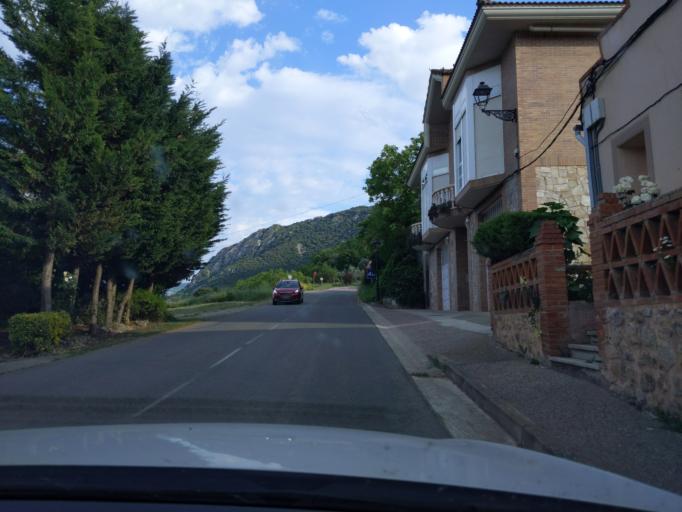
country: ES
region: La Rioja
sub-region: Provincia de La Rioja
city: Clavijo
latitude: 42.3659
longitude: -2.4211
